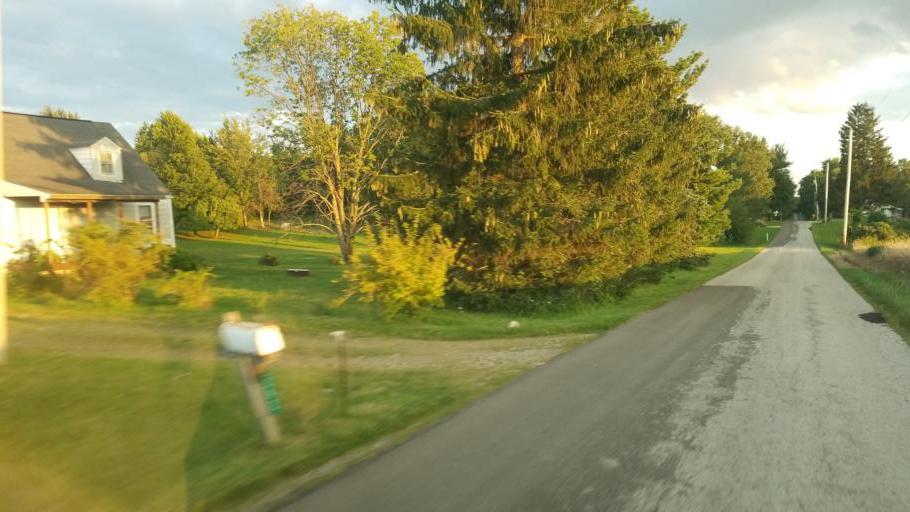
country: US
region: Ohio
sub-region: Richland County
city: Mansfield
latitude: 40.8205
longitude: -82.5422
